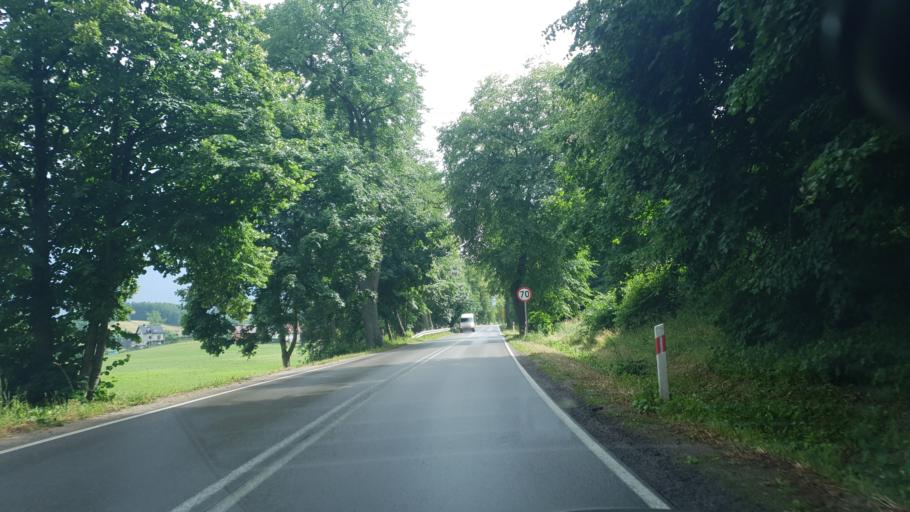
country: PL
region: Pomeranian Voivodeship
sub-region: Powiat kartuski
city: Chmielno
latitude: 54.3076
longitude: 18.1497
